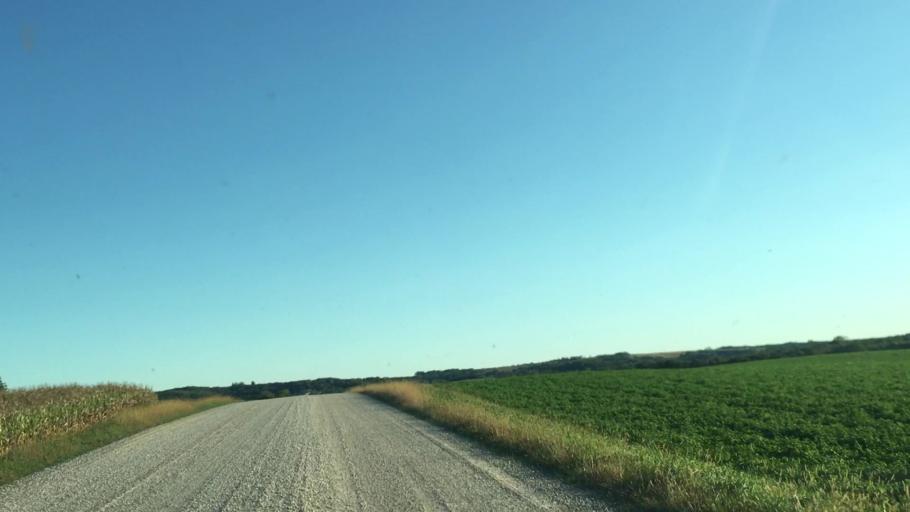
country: US
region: Minnesota
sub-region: Fillmore County
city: Preston
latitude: 43.7684
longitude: -92.0294
